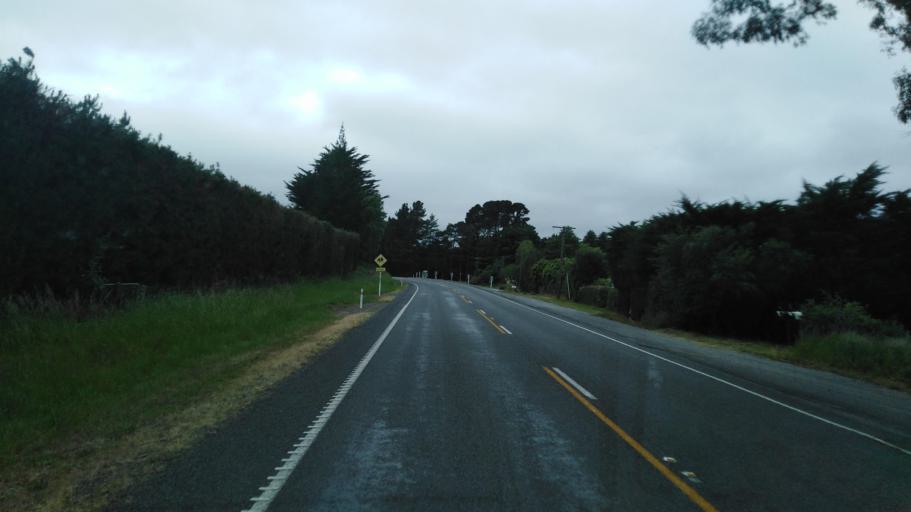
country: NZ
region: Canterbury
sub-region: Hurunui District
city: Amberley
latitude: -42.9641
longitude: 172.9755
